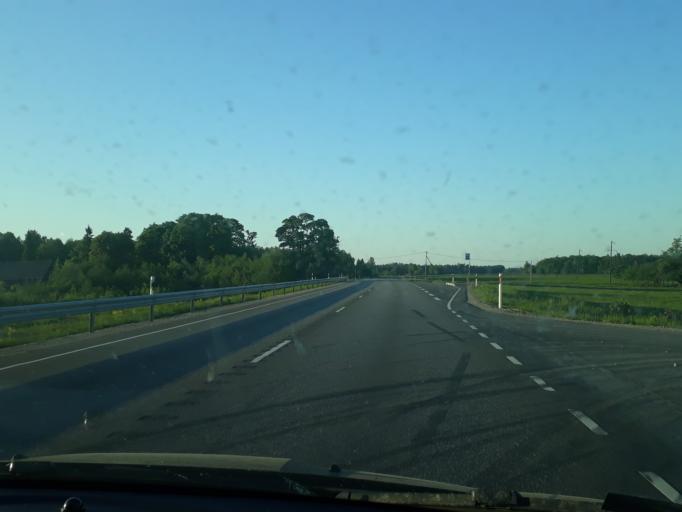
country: EE
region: Paernumaa
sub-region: Tootsi vald
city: Tootsi
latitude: 58.5652
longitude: 24.8720
